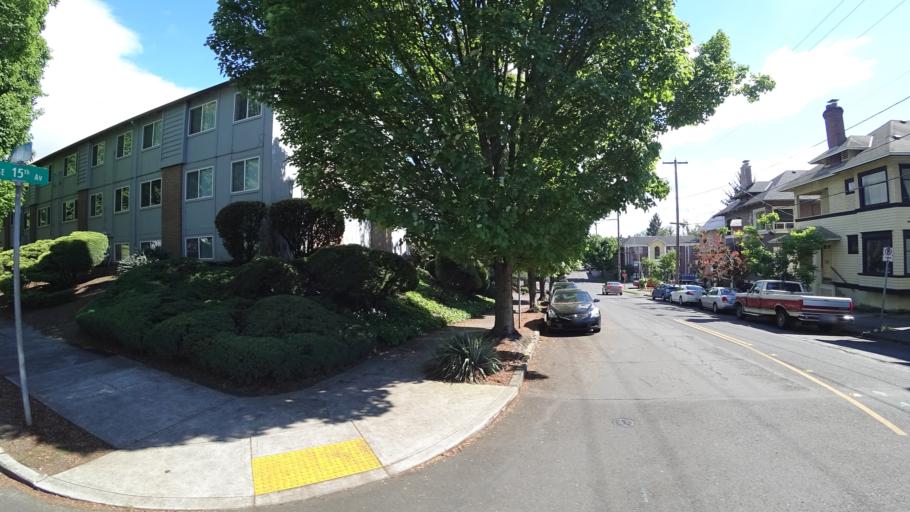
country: US
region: Oregon
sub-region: Multnomah County
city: Portland
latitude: 45.5200
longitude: -122.6506
